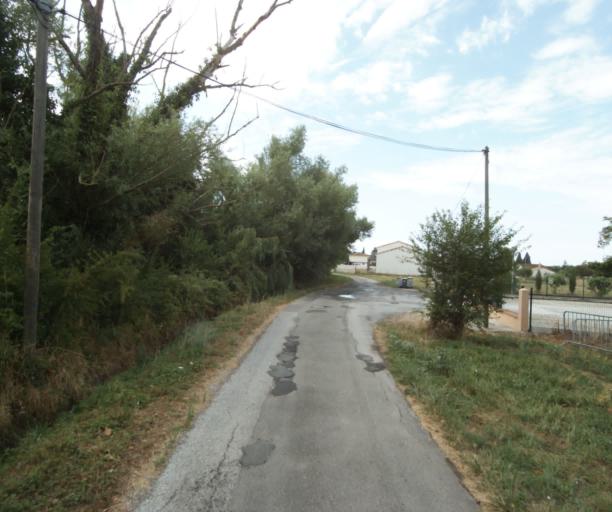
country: FR
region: Midi-Pyrenees
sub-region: Departement de la Haute-Garonne
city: Revel
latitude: 43.4681
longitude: 2.0007
